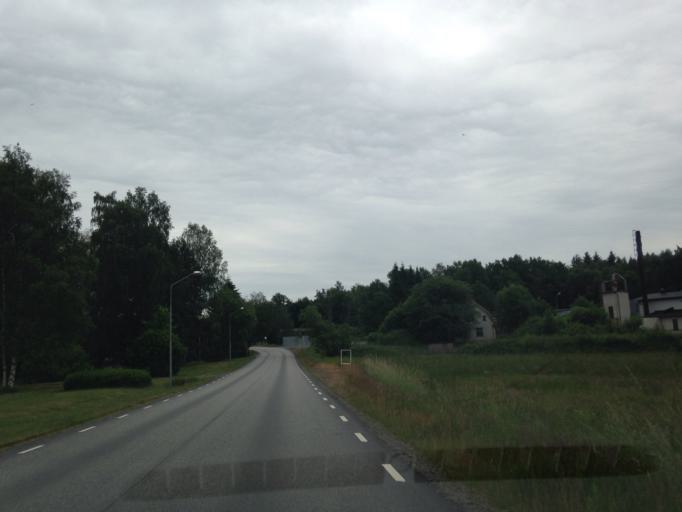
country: SE
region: Vaestra Goetaland
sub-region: Marks Kommun
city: Horred
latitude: 57.4708
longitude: 12.4825
